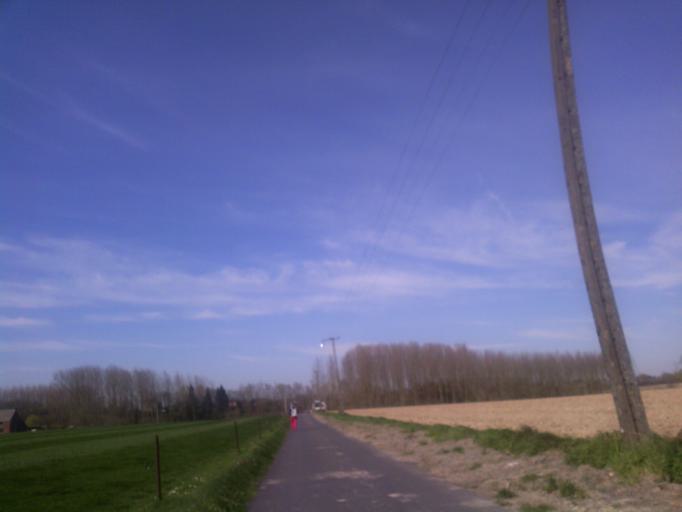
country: BE
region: Wallonia
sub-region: Province du Hainaut
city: Silly
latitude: 50.6678
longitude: 3.9235
